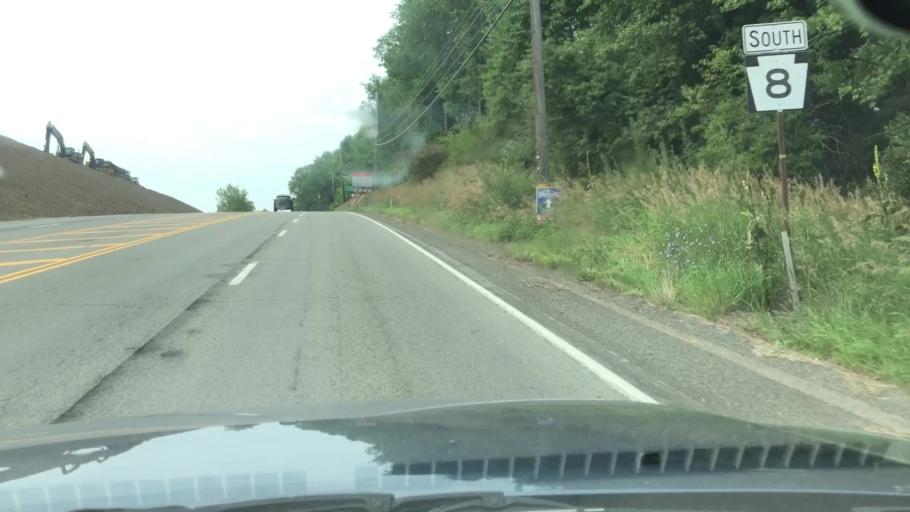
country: US
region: Pennsylvania
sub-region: Allegheny County
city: Bakerstown
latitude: 40.7012
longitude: -79.9367
